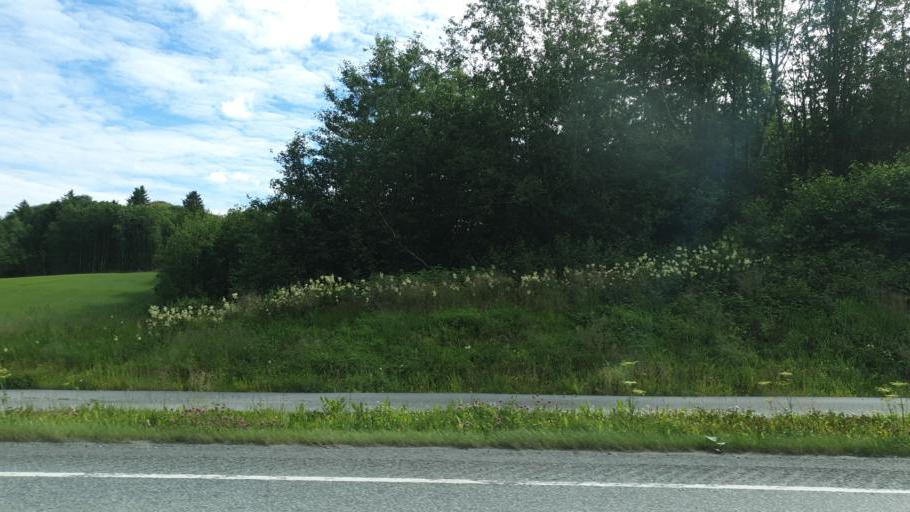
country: NO
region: Sor-Trondelag
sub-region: Melhus
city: Lundamo
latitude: 63.1758
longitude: 10.3167
